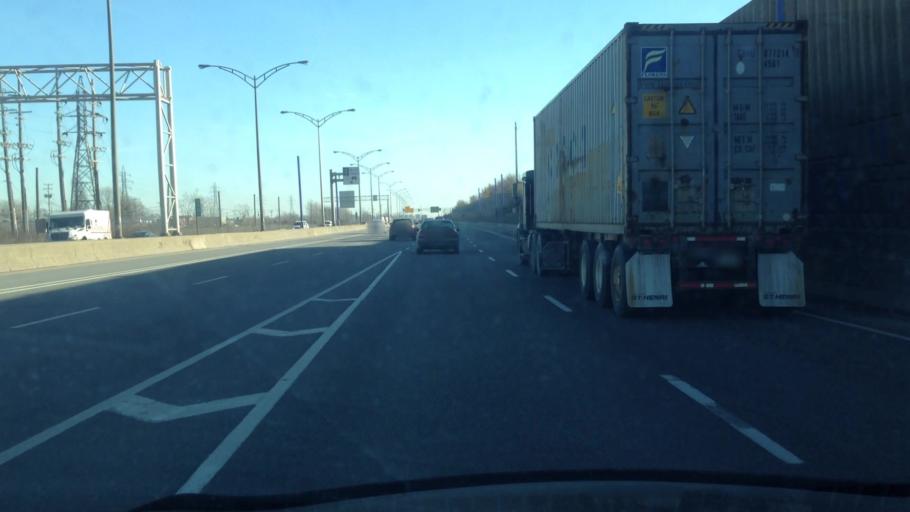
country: CA
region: Quebec
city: Cote-Saint-Luc
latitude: 45.4474
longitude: -73.6864
